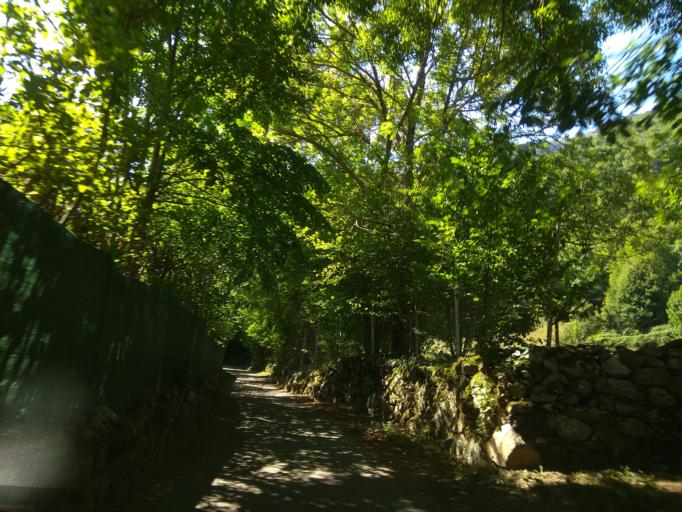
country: ES
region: Catalonia
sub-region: Provincia de Lleida
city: Les
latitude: 42.7552
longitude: 0.6941
